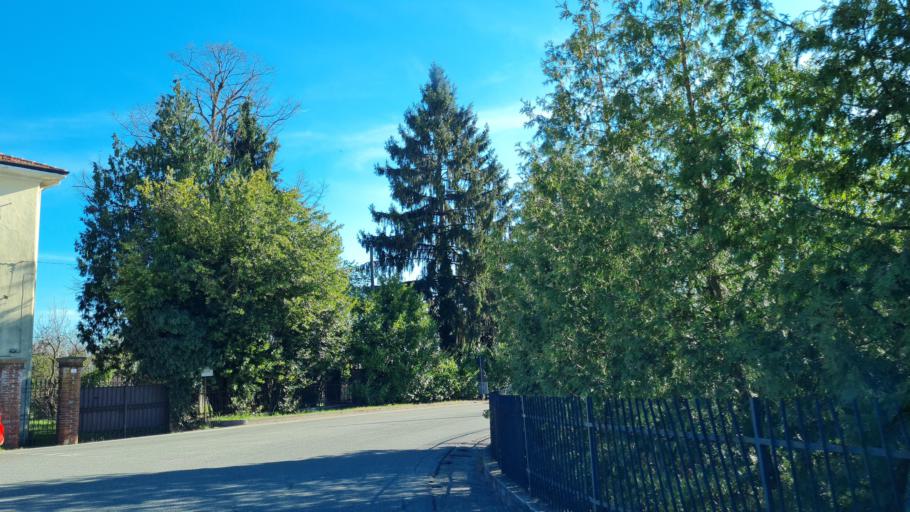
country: IT
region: Piedmont
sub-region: Provincia di Novara
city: Maggiora
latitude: 45.6879
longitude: 8.4274
